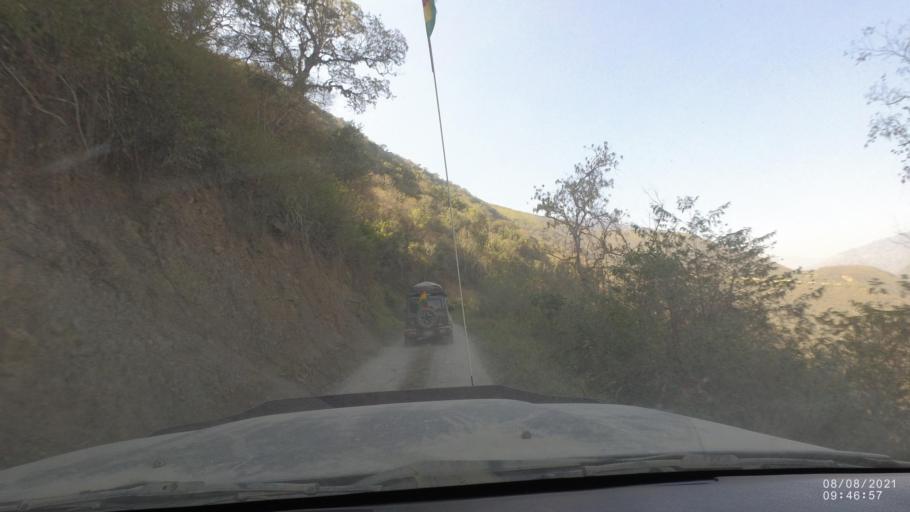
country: BO
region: La Paz
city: Quime
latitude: -16.6076
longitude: -66.7299
